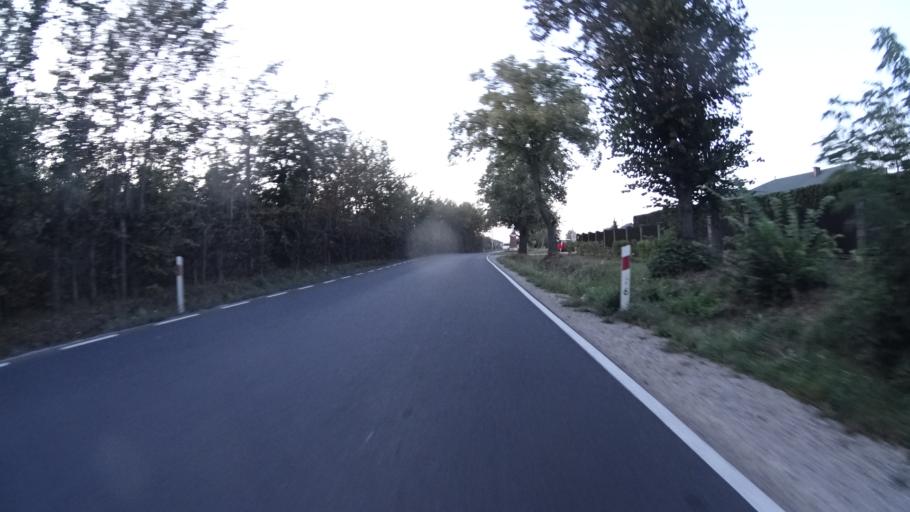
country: PL
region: Masovian Voivodeship
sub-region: Powiat warszawski zachodni
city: Ozarow Mazowiecki
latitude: 52.2296
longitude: 20.7715
